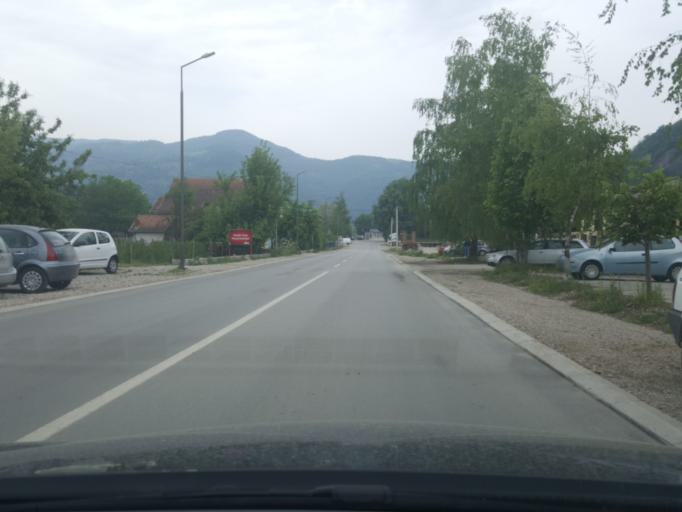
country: RS
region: Central Serbia
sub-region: Zlatiborski Okrug
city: Bajina Basta
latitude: 43.9827
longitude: 19.5688
